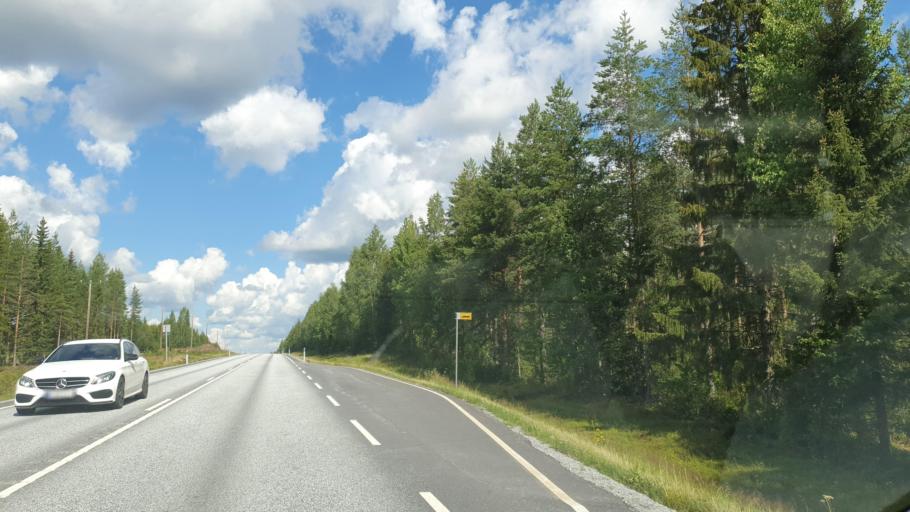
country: FI
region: Northern Savo
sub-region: Ylae-Savo
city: Sonkajaervi
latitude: 63.9558
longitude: 27.3753
